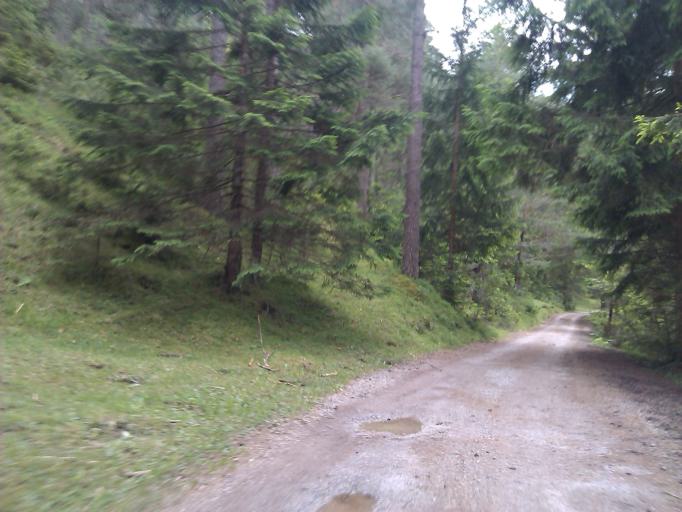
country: AT
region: Tyrol
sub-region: Politischer Bezirk Imst
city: Nassereith
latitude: 47.2873
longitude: 10.8344
